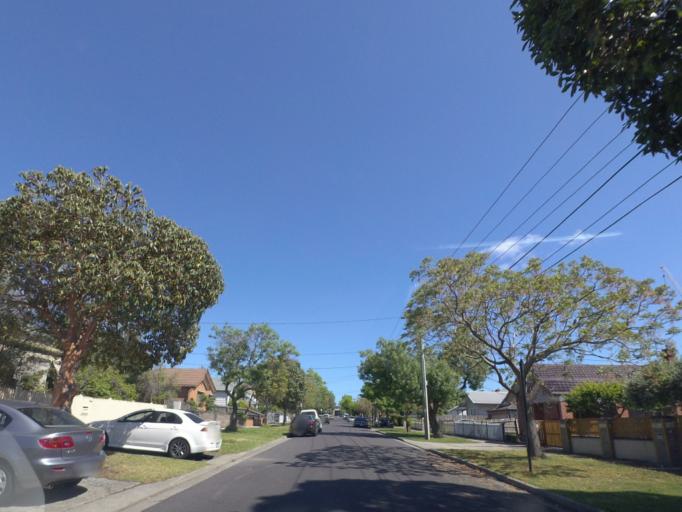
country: AU
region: Victoria
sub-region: Monash
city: Chadstone
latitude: -37.8975
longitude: 145.0968
